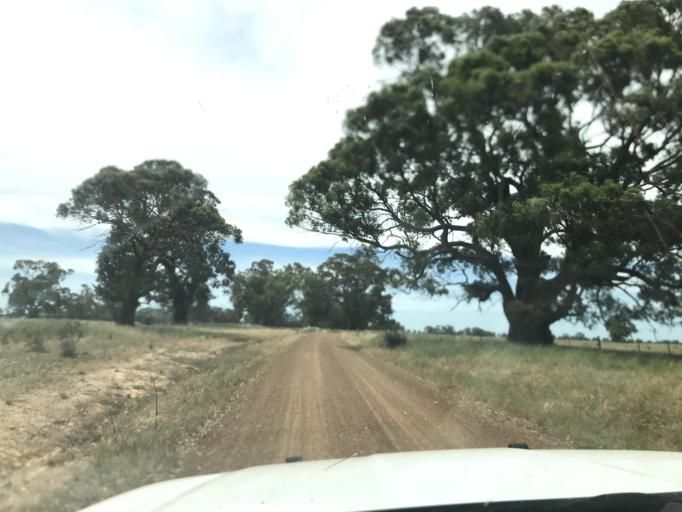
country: AU
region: South Australia
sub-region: Wattle Range
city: Penola
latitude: -37.0147
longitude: 141.4771
